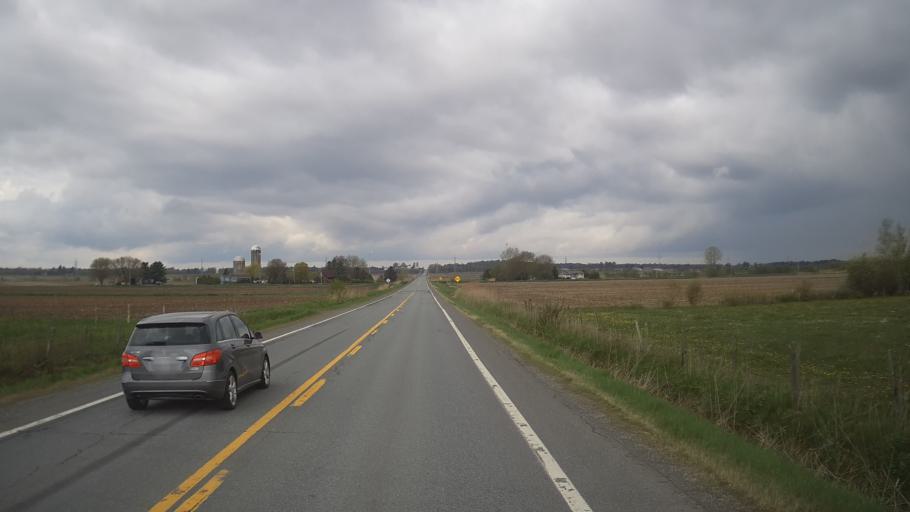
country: CA
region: Quebec
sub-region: Monteregie
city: Farnham
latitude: 45.2561
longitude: -72.9145
